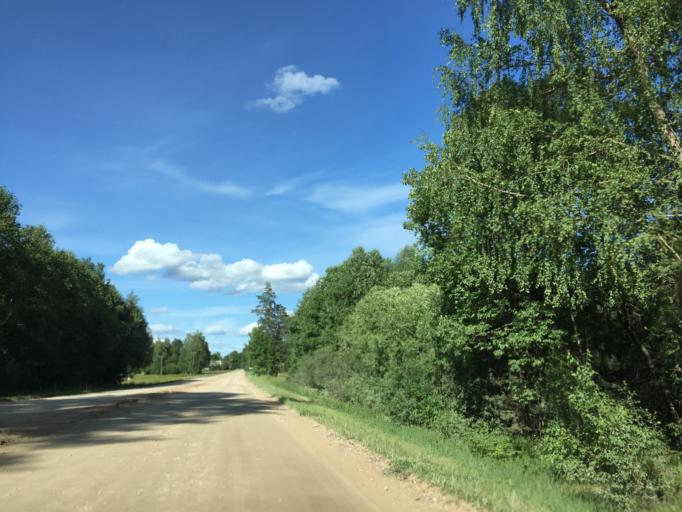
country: LV
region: Vecumnieki
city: Vecumnieki
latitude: 56.4485
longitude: 24.5866
